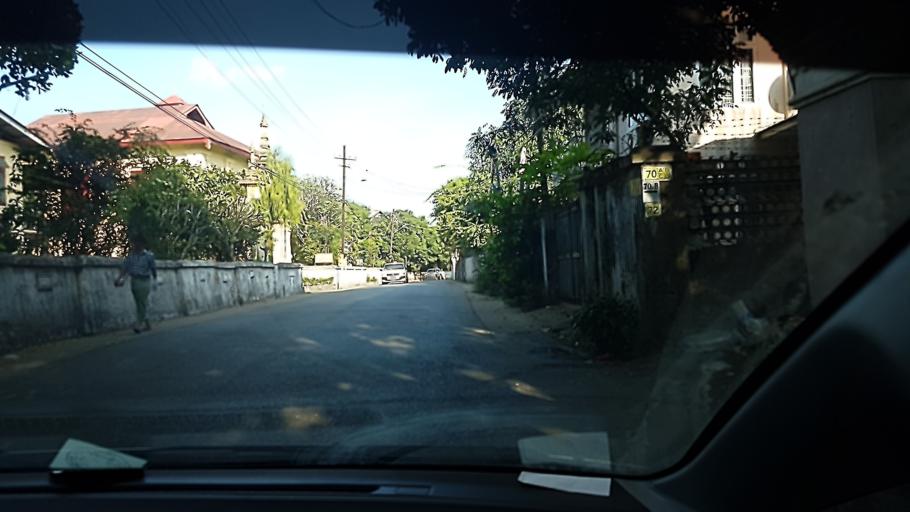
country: MM
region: Yangon
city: Yangon
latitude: 16.8134
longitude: 96.1609
